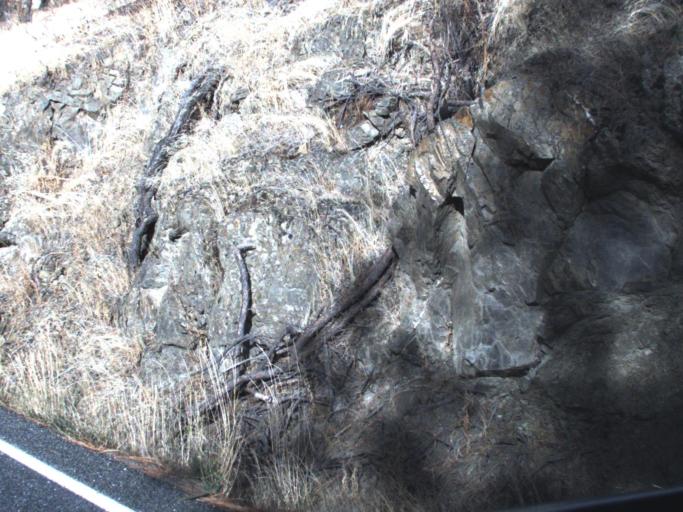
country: US
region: Washington
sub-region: Stevens County
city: Kettle Falls
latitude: 48.3327
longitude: -118.1553
